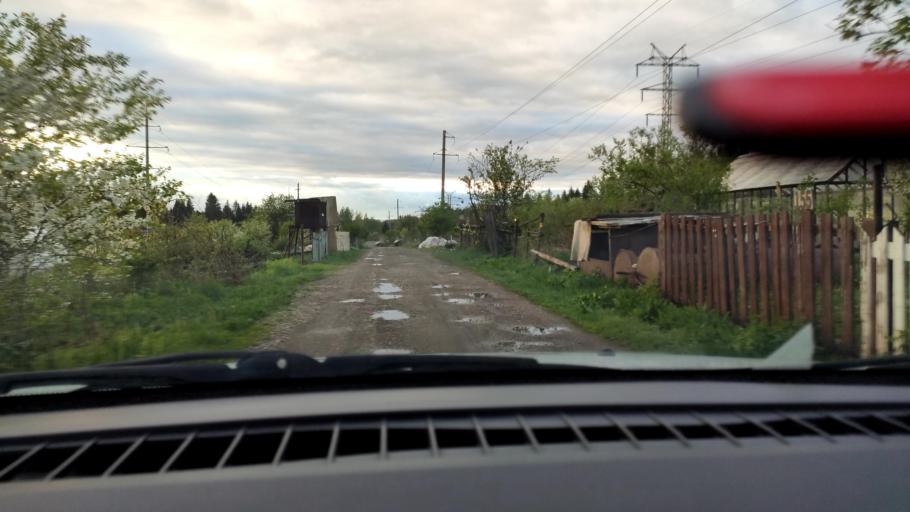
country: RU
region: Perm
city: Polazna
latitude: 58.1304
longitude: 56.4136
